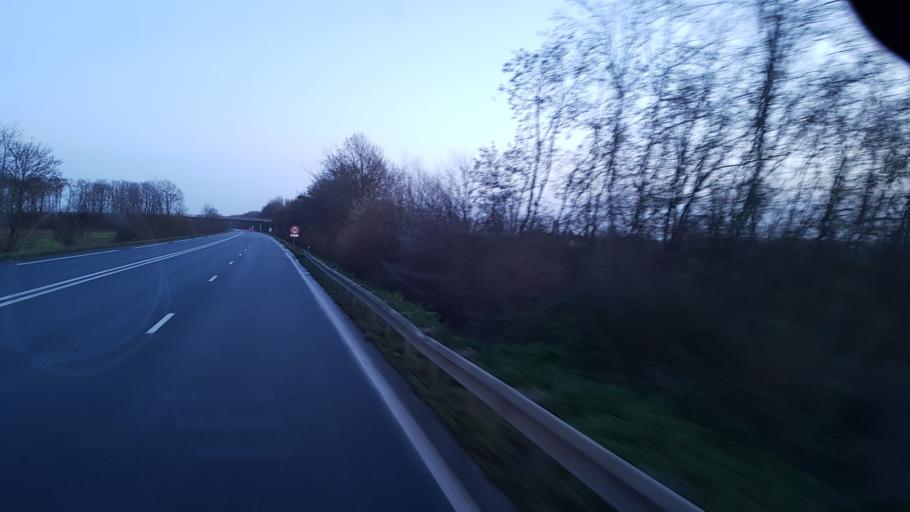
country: FR
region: Nord-Pas-de-Calais
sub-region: Departement du Nord
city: Ferin
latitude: 50.3345
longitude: 3.0913
